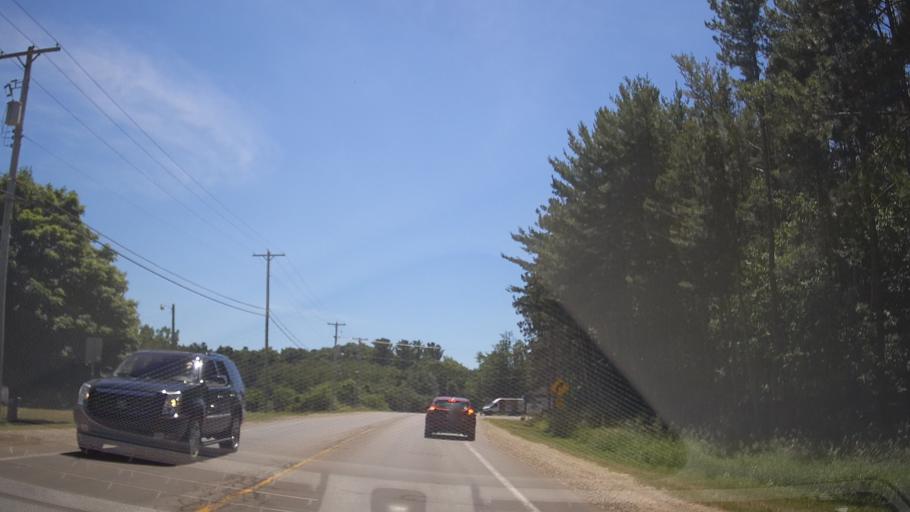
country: US
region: Michigan
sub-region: Grand Traverse County
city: Traverse City
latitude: 44.7169
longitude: -85.6851
